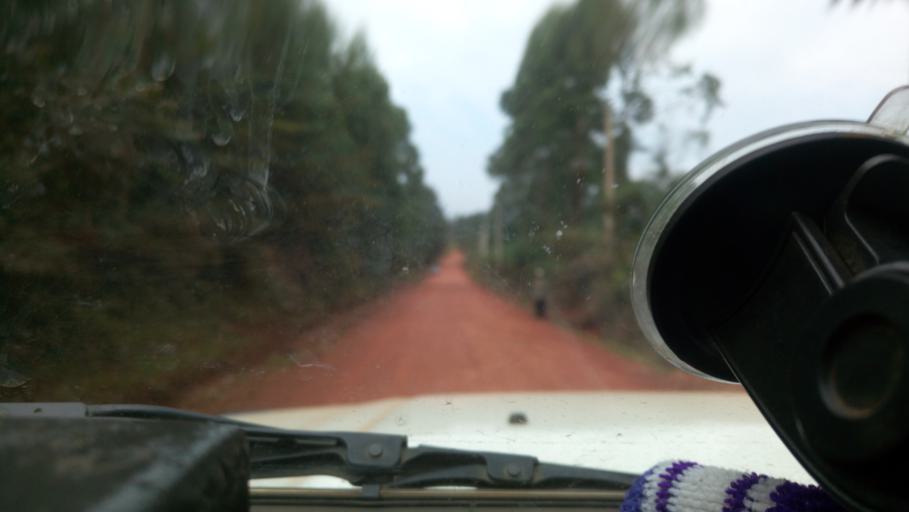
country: KE
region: Kericho
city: Litein
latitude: -0.6087
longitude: 35.2240
